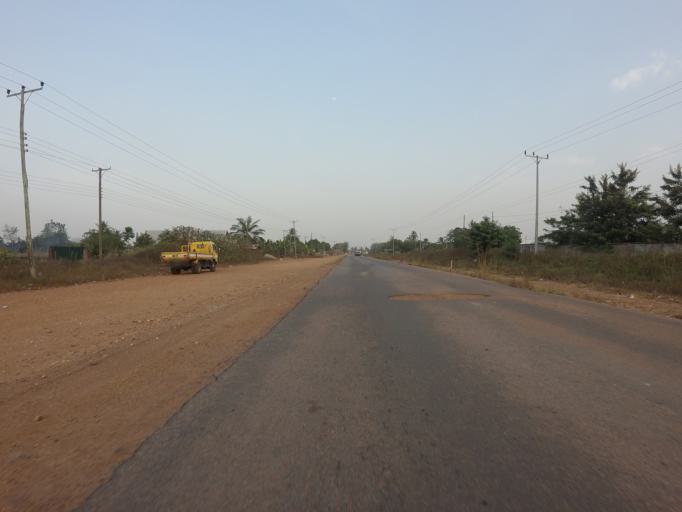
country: GH
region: Volta
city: Ho
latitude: 6.5733
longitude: 0.4083
